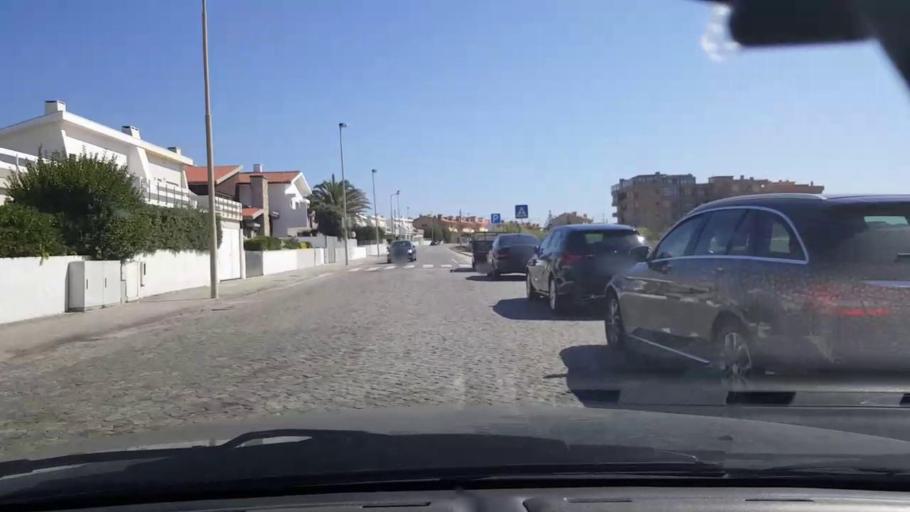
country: PT
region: Porto
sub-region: Vila do Conde
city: Arvore
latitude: 41.3041
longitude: -8.7371
